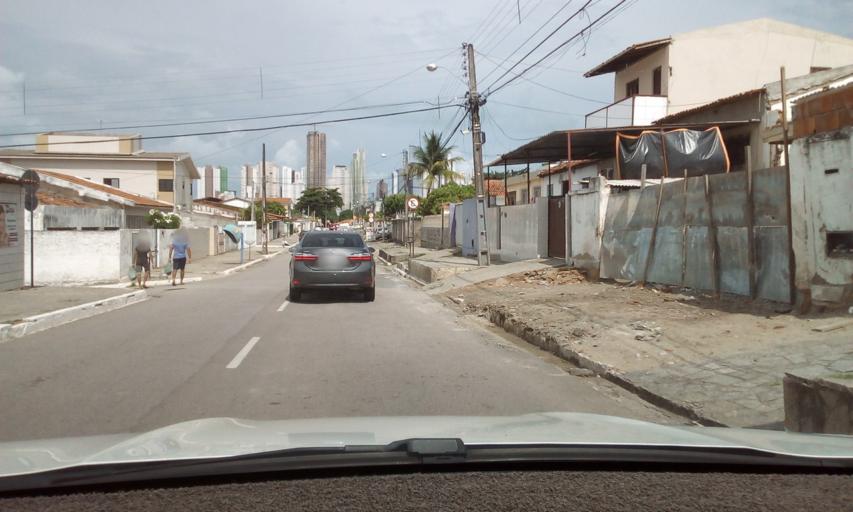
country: BR
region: Paraiba
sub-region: Joao Pessoa
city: Joao Pessoa
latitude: -7.1307
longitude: -34.8423
